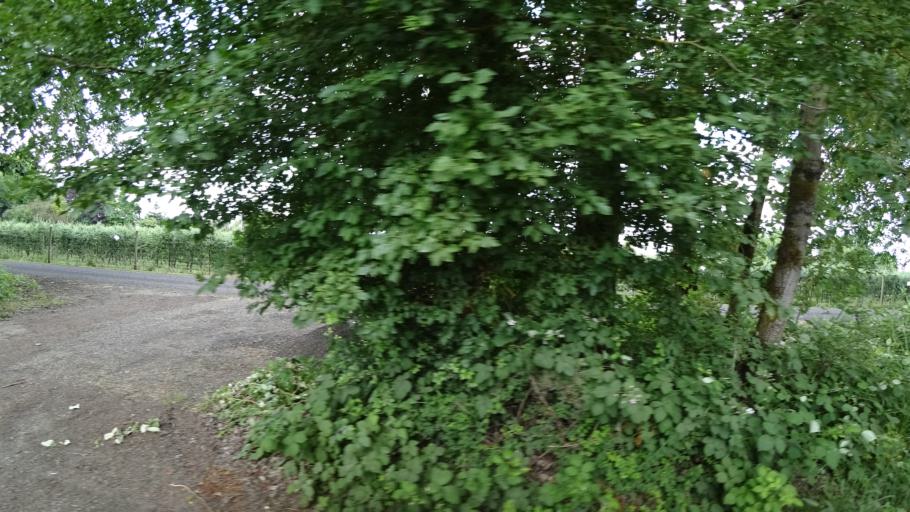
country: US
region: Oregon
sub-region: Washington County
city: Oak Hills
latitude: 45.6299
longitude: -122.8000
